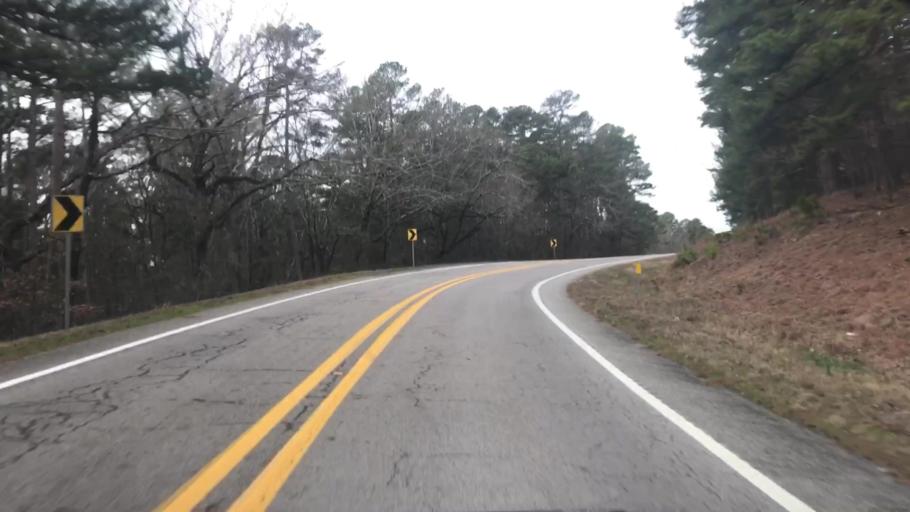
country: US
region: Arkansas
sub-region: Montgomery County
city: Mount Ida
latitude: 34.6707
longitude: -93.7798
